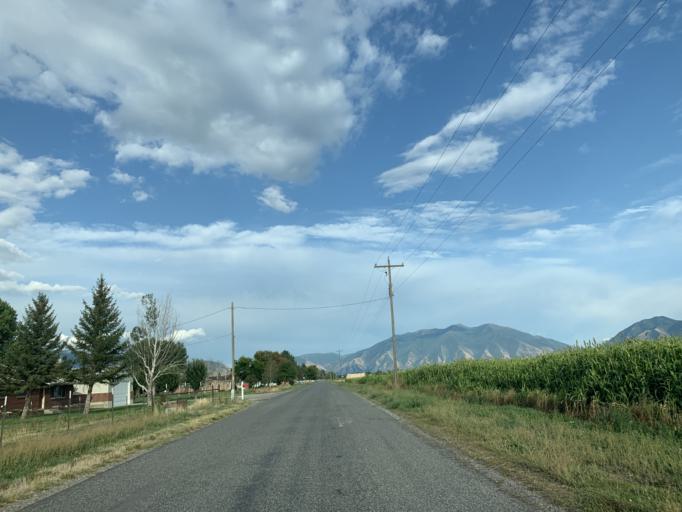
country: US
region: Utah
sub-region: Utah County
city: Benjamin
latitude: 40.1290
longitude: -111.7566
